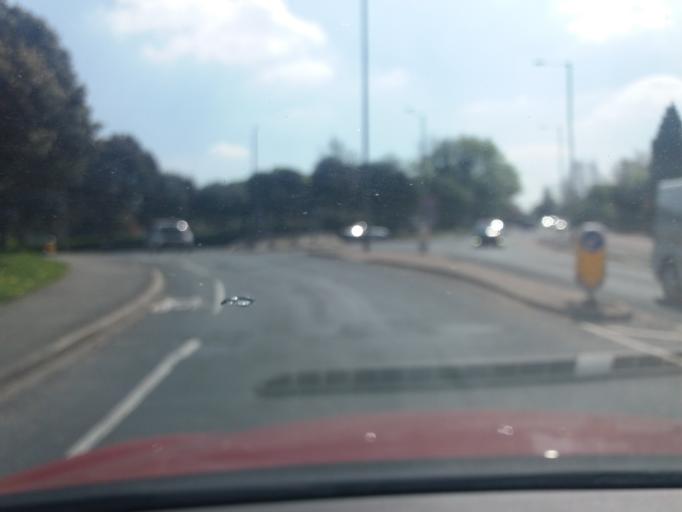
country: GB
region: England
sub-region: Lancashire
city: Chorley
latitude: 53.6780
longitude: -2.6357
